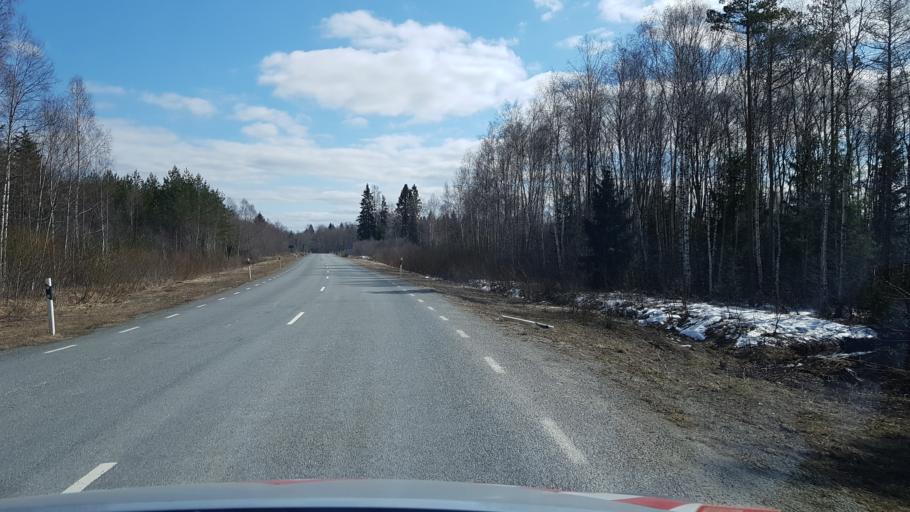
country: EE
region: Laeaene-Virumaa
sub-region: Tapa vald
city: Tapa
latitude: 59.2743
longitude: 25.9153
